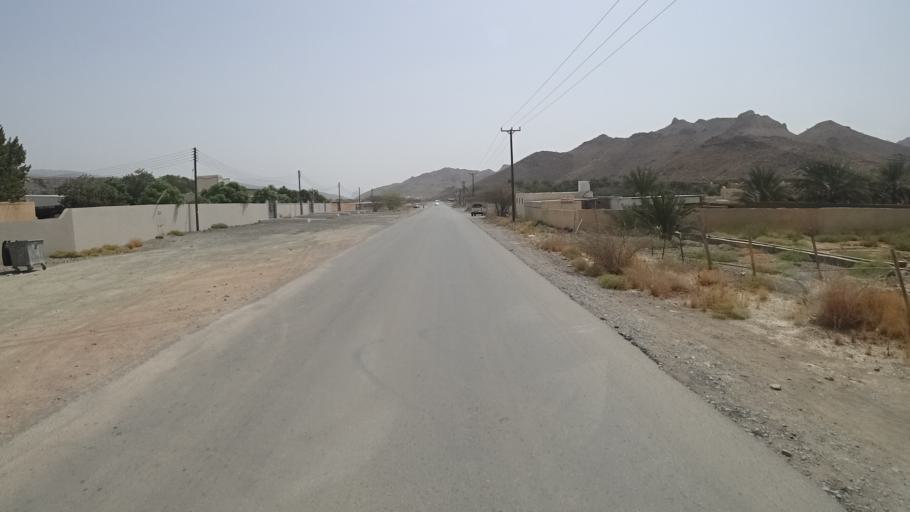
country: OM
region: Muhafazat ad Dakhiliyah
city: Bahla'
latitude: 23.0841
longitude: 57.3205
